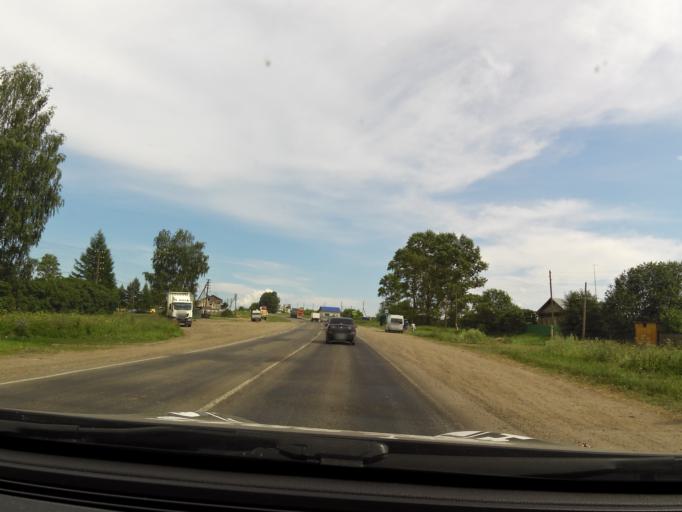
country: RU
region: Kirov
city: Vakhrushi
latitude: 58.6769
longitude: 50.0044
